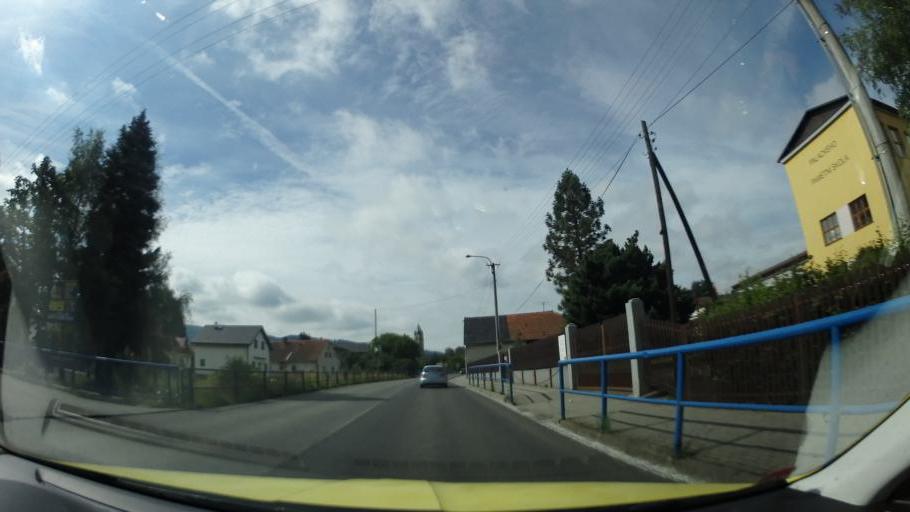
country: CZ
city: Hodslavice
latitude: 49.5415
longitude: 18.0257
